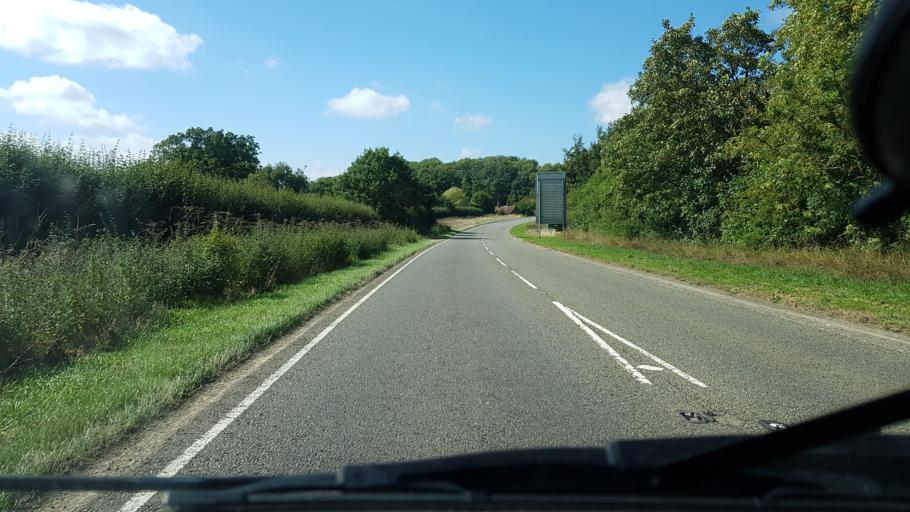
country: GB
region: England
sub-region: West Sussex
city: Horsham
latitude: 51.0883
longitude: -0.3359
